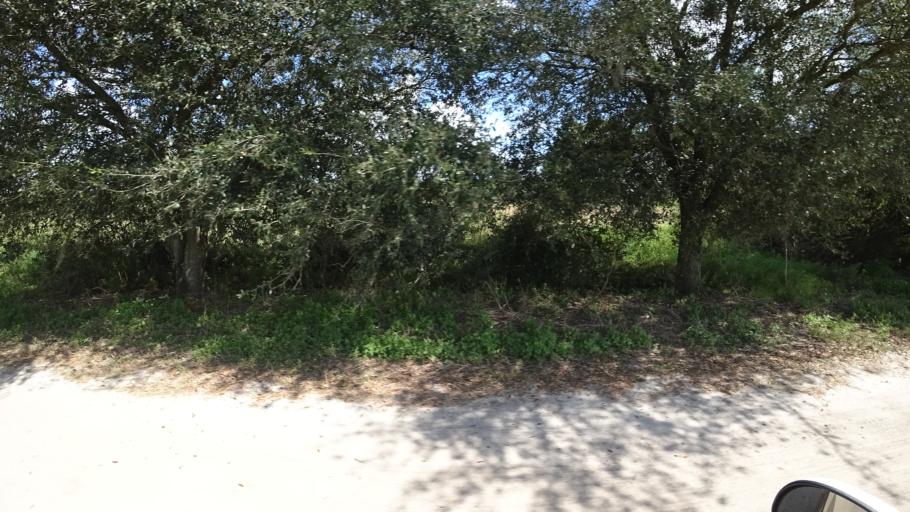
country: US
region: Florida
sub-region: Sarasota County
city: Warm Mineral Springs
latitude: 27.3175
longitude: -82.1304
